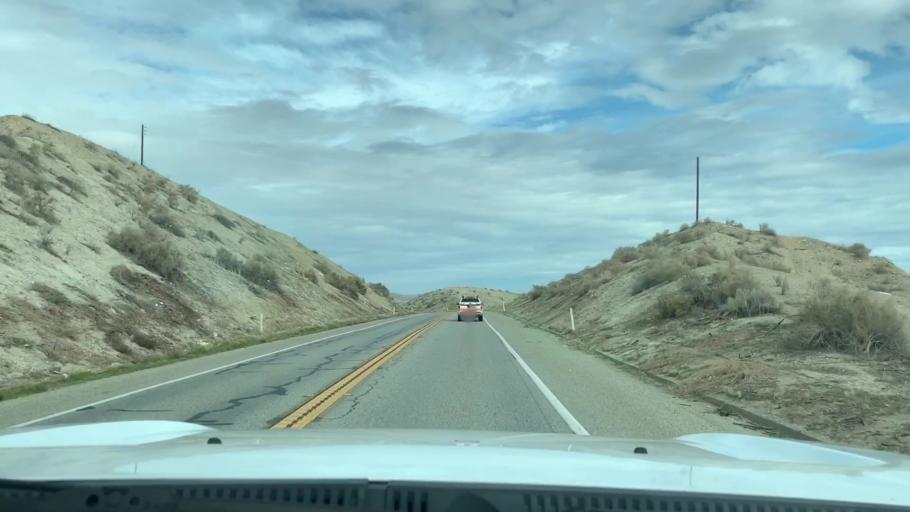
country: US
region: California
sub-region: Kern County
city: Maricopa
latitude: 35.0782
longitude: -119.4013
